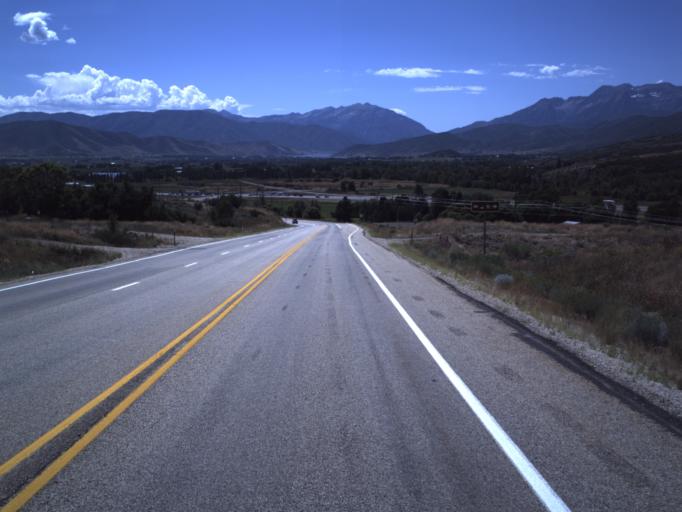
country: US
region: Utah
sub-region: Wasatch County
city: Heber
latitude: 40.5654
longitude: -111.4224
